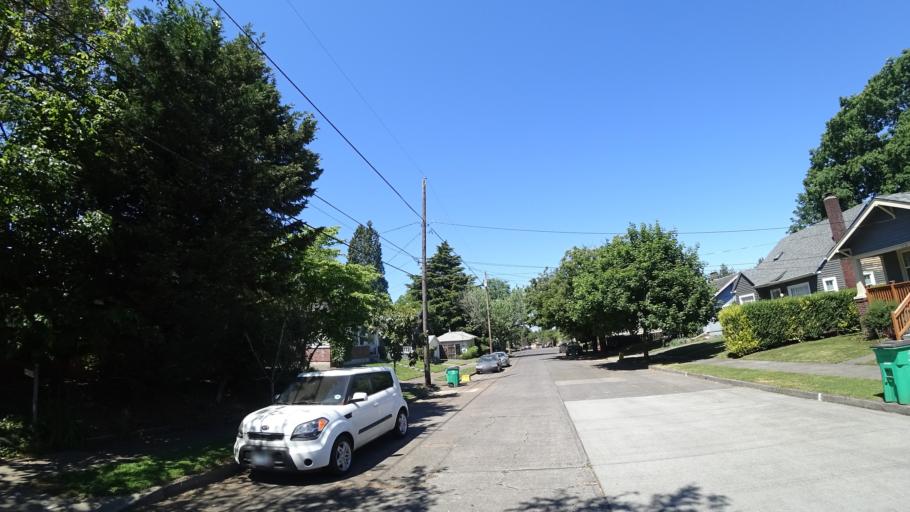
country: US
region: Oregon
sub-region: Multnomah County
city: Portland
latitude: 45.5656
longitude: -122.6480
